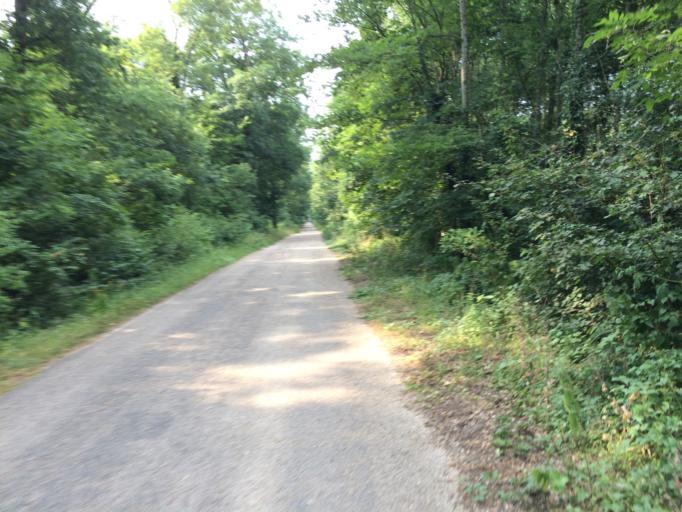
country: FR
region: Ile-de-France
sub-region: Departement de l'Essonne
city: Bievres
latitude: 48.7700
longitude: 2.2358
